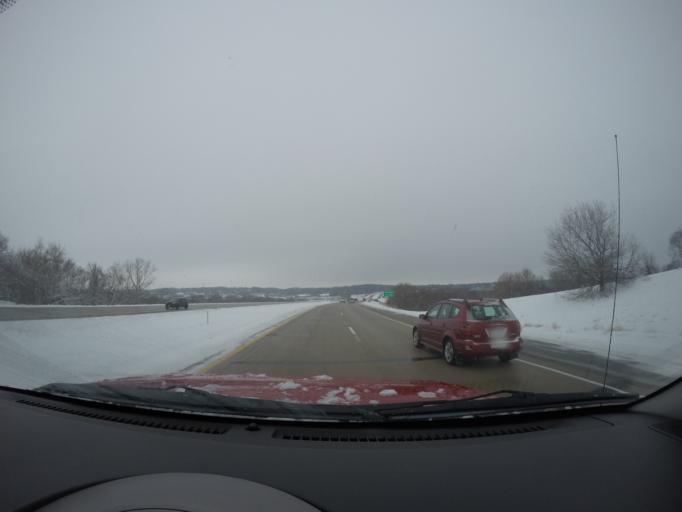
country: US
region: Minnesota
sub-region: Olmsted County
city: Rochester
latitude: 43.9739
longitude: -92.4492
